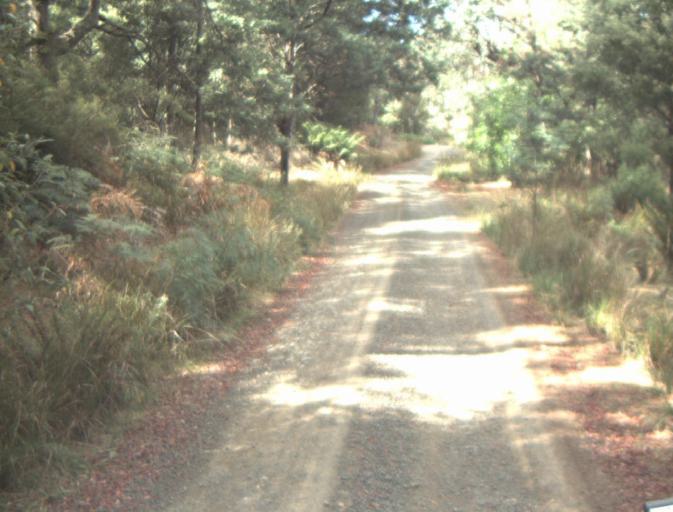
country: AU
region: Tasmania
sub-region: Launceston
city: Mayfield
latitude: -41.2794
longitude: 147.2326
